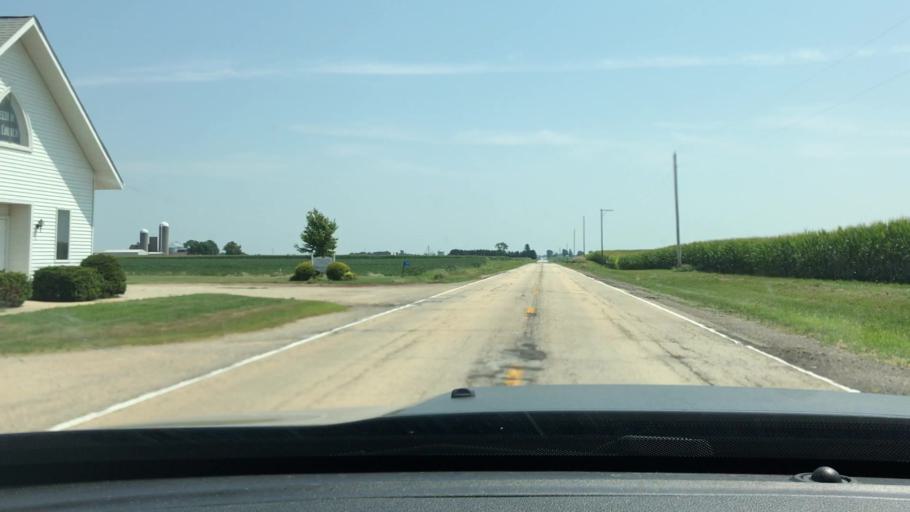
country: US
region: Illinois
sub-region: LaSalle County
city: Ottawa
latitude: 41.4701
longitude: -88.8683
